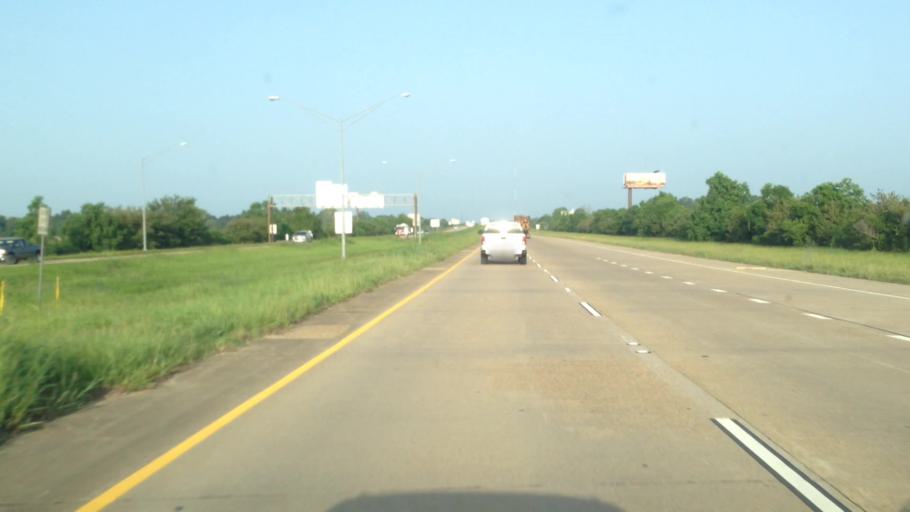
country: US
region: Louisiana
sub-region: Rapides Parish
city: Alexandria
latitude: 31.2402
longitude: -92.4370
